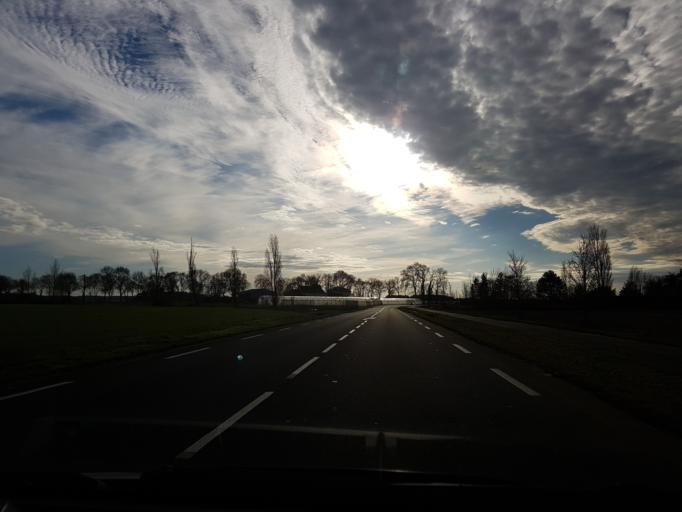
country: FR
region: Centre
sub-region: Departement du Loiret
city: Saint-Denis-en-Val
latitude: 47.8641
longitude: 1.9826
